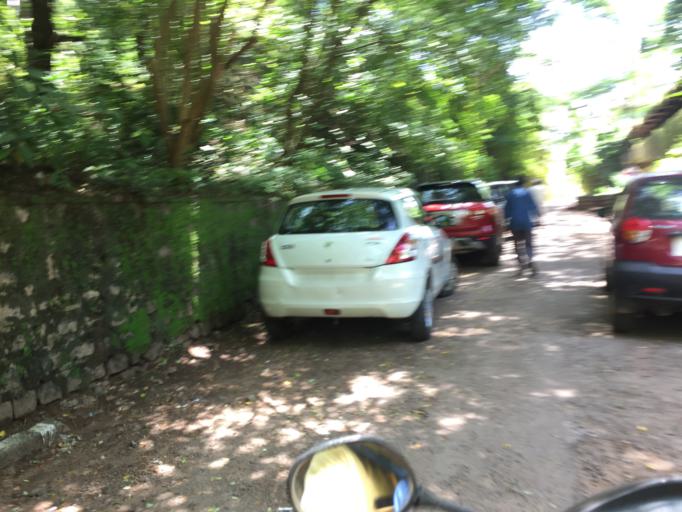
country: IN
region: Karnataka
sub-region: Dakshina Kannada
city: Mangalore
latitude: 12.8751
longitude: 74.8419
